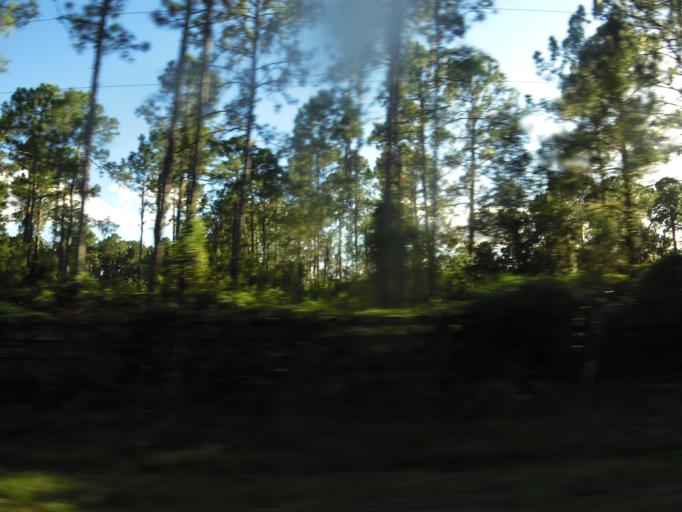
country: US
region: Florida
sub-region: Marion County
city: Citra
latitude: 29.4560
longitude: -82.1312
